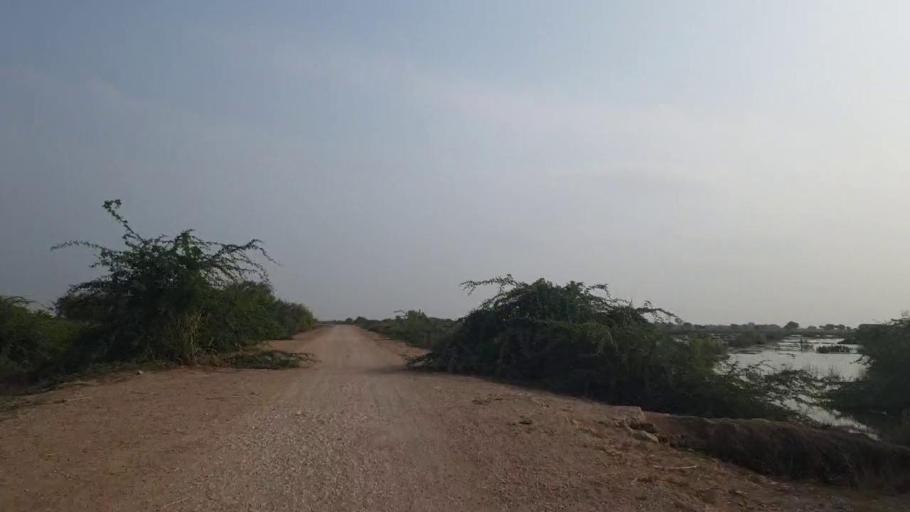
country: PK
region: Sindh
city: Badin
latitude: 24.6024
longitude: 68.6960
